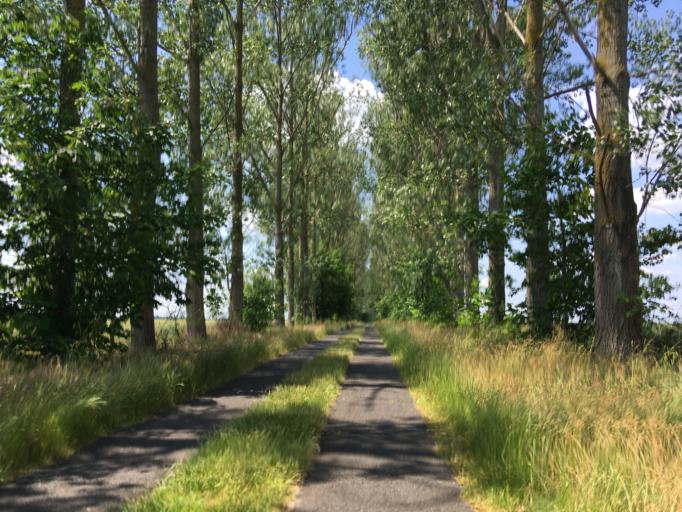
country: DE
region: Brandenburg
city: Werftpfuhl
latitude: 52.6890
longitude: 13.7574
